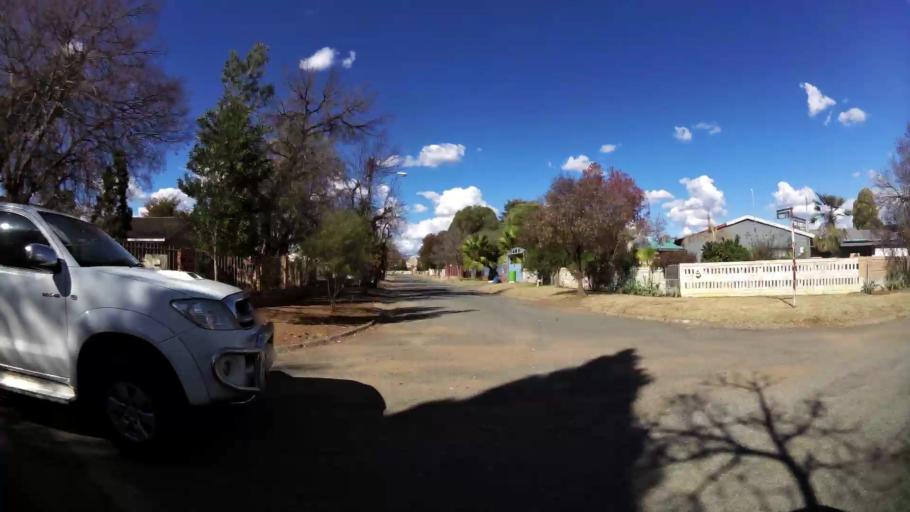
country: ZA
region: North-West
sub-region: Dr Kenneth Kaunda District Municipality
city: Klerksdorp
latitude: -26.8596
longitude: 26.6384
